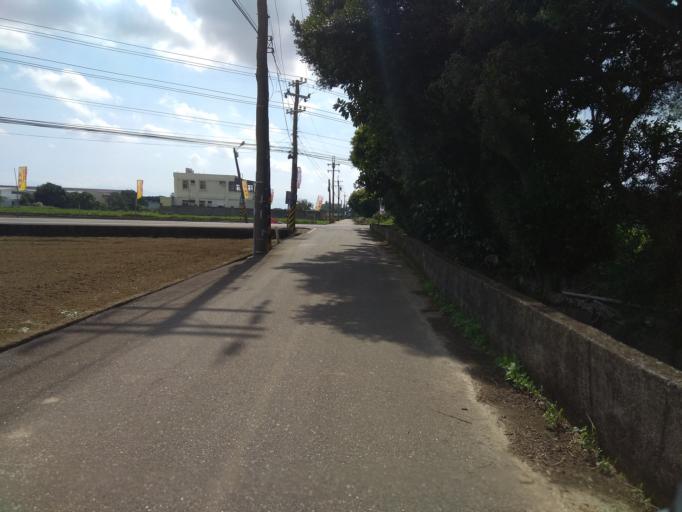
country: TW
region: Taiwan
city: Taoyuan City
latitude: 25.0730
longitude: 121.2489
